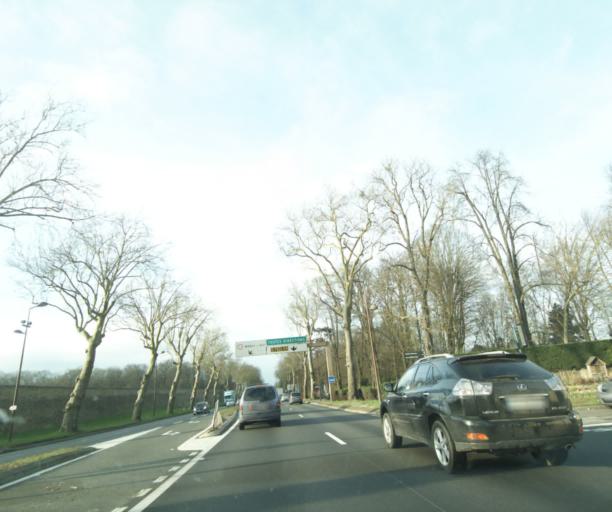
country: FR
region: Ile-de-France
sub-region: Departement des Yvelines
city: Louveciennes
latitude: 48.8555
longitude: 2.1074
